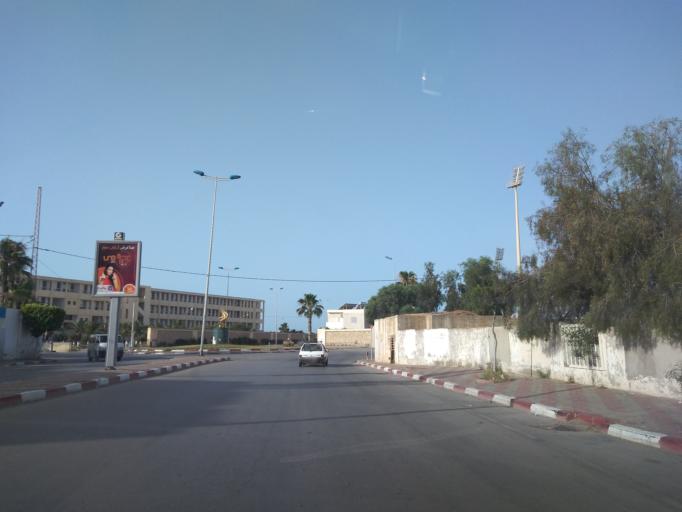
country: TN
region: Safaqis
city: Sfax
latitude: 34.7347
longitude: 10.7484
